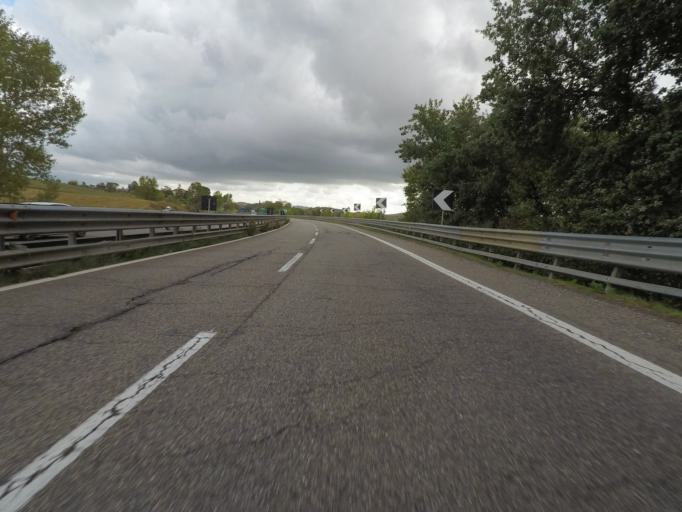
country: IT
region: Tuscany
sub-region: Provincia di Siena
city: Taverne D'Arbia
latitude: 43.2959
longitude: 11.3919
